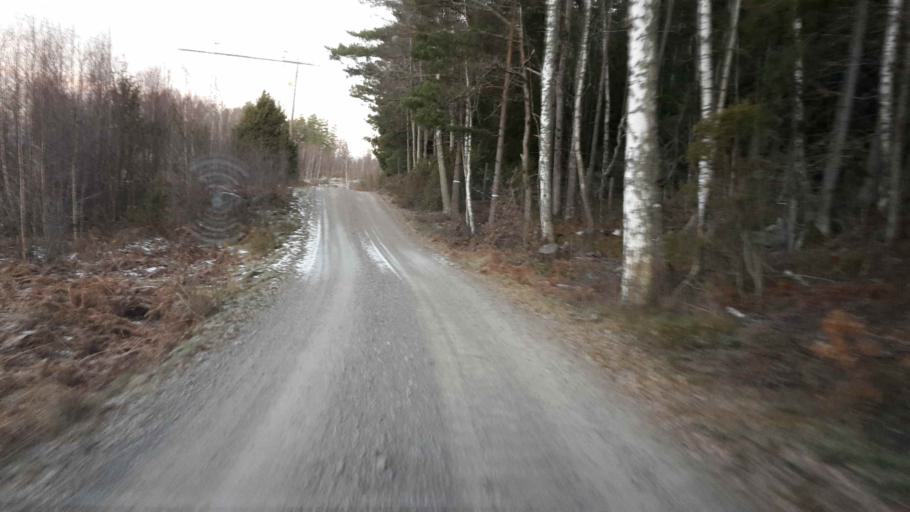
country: SE
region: OEstergoetland
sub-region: Atvidabergs Kommun
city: Atvidaberg
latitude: 58.2644
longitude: 16.1361
